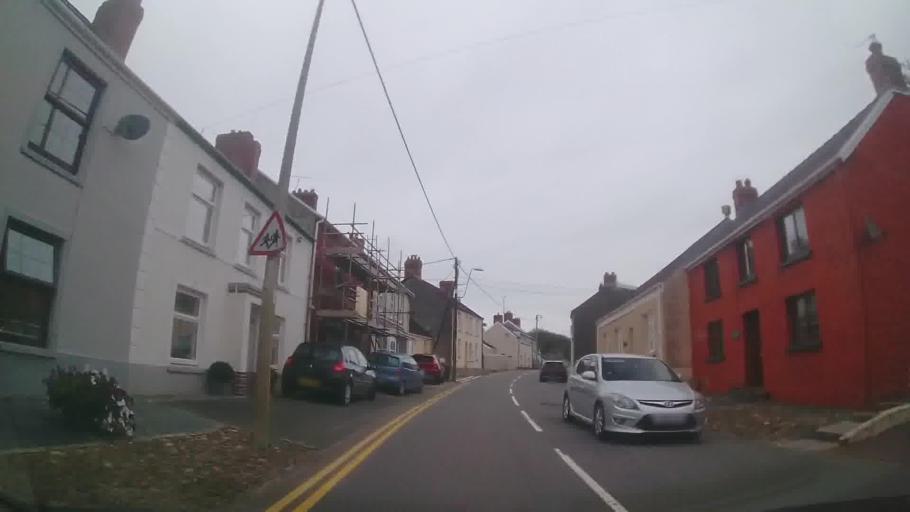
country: GB
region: Wales
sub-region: Carmarthenshire
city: Saint Clears
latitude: 51.8104
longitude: -4.4957
